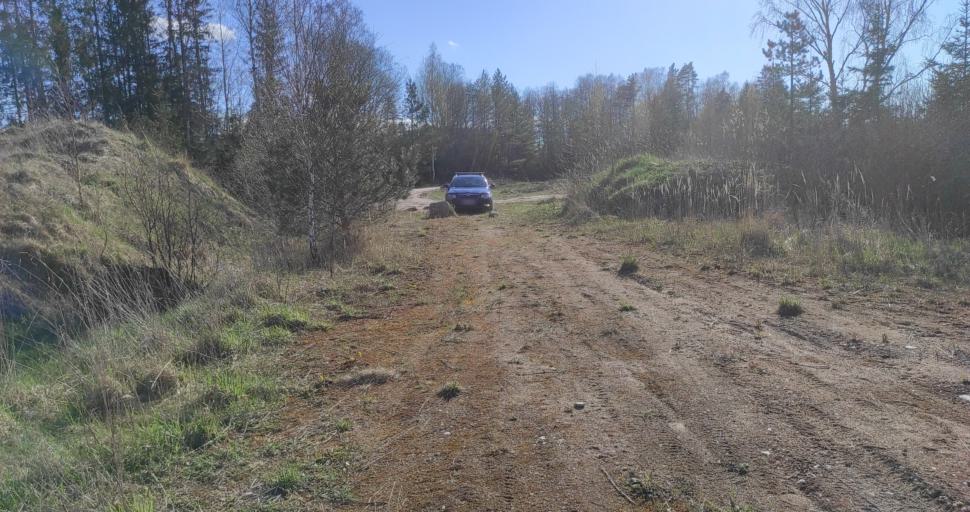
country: LV
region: Kuldigas Rajons
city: Kuldiga
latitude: 56.8963
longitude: 21.8664
